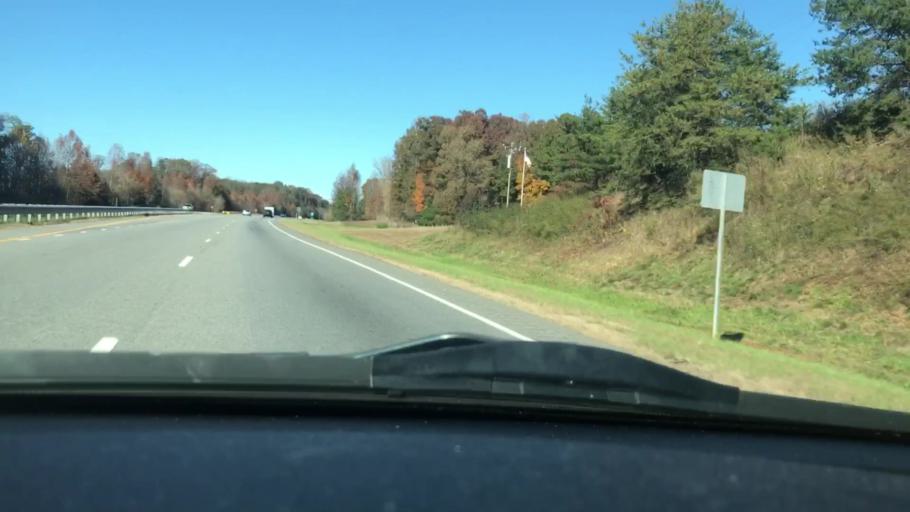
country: US
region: North Carolina
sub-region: Rockingham County
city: Madison
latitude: 36.3898
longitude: -79.9411
